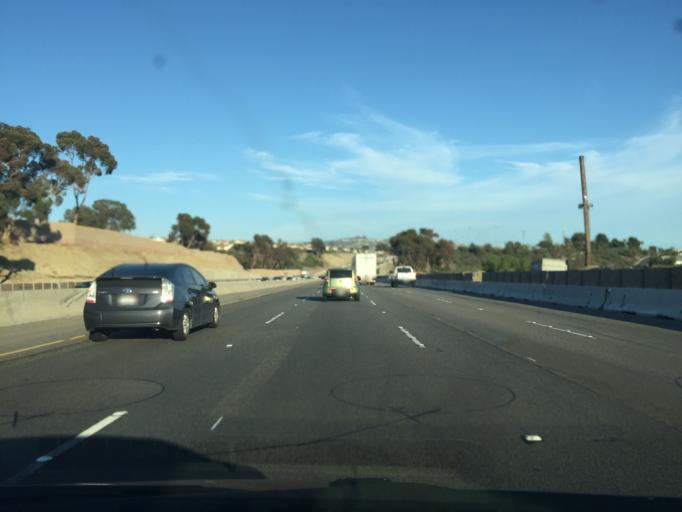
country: US
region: California
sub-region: Orange County
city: San Clemente
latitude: 33.4548
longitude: -117.6484
